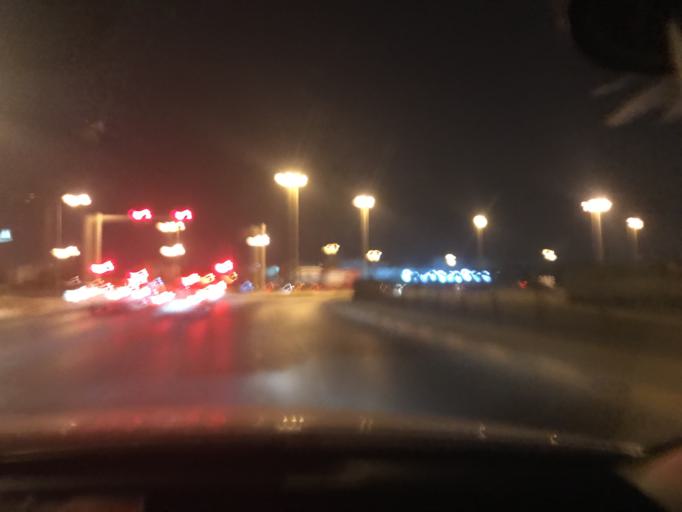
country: BH
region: Muharraq
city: Al Hadd
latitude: 26.2558
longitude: 50.6551
